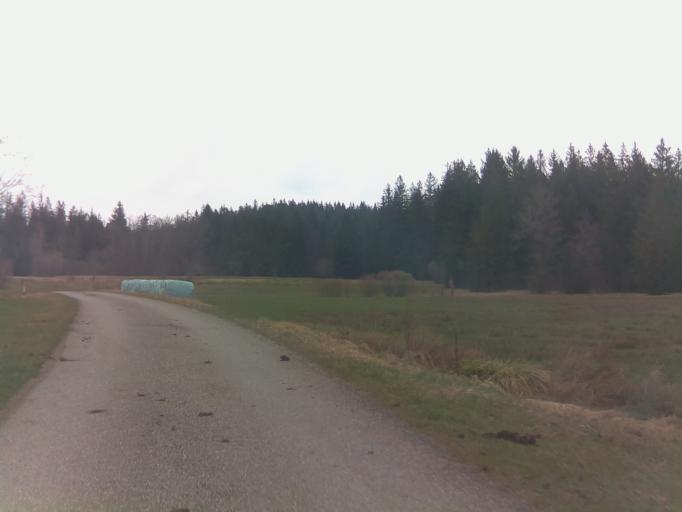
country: DE
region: Bavaria
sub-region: Upper Bavaria
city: Bobing
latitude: 47.7349
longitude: 11.0485
